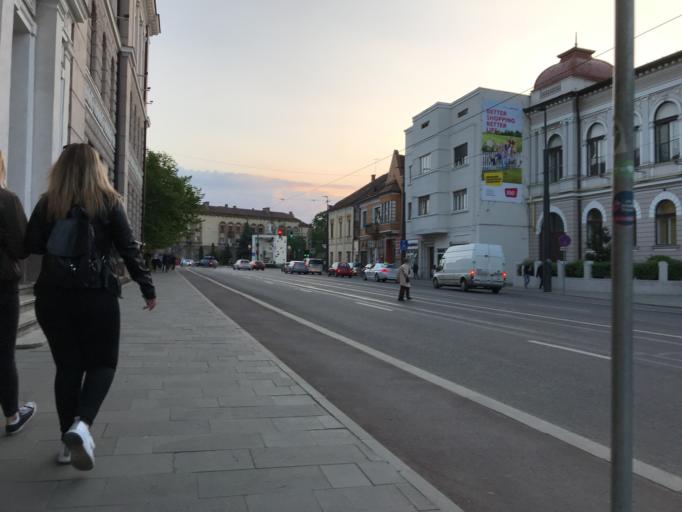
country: RO
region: Cluj
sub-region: Municipiul Cluj-Napoca
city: Cluj-Napoca
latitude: 46.7723
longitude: 23.5856
